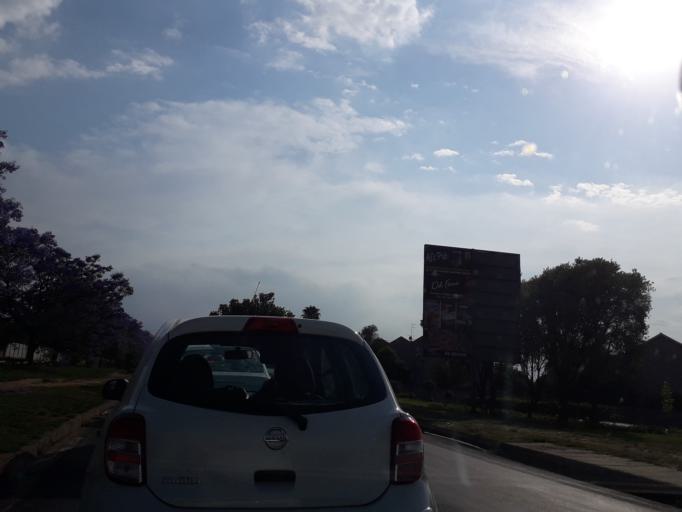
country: ZA
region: Gauteng
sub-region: City of Johannesburg Metropolitan Municipality
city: Roodepoort
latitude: -26.1135
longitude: 27.9465
